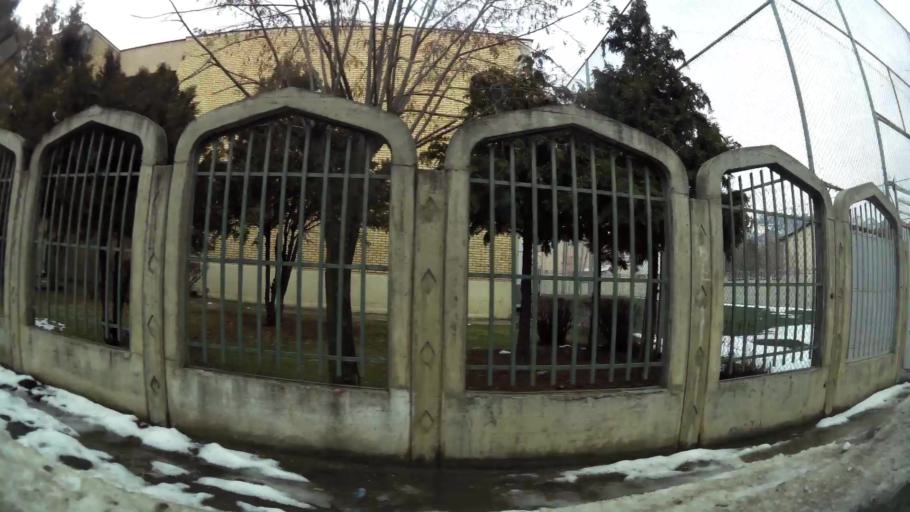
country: XK
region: Pristina
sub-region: Komuna e Prishtines
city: Pristina
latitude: 42.6734
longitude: 21.1688
